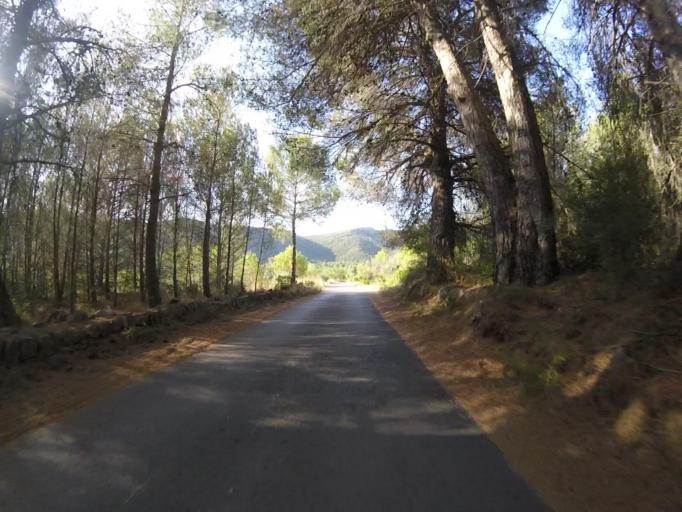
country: ES
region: Valencia
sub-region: Provincia de Castello
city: Cabanes
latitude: 40.1056
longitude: 0.0645
